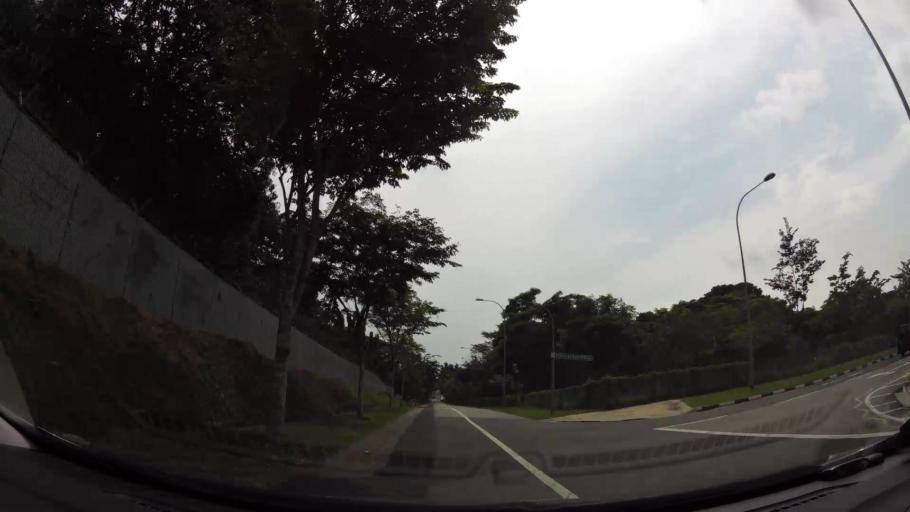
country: SG
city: Singapore
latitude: 1.3599
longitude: 103.9763
